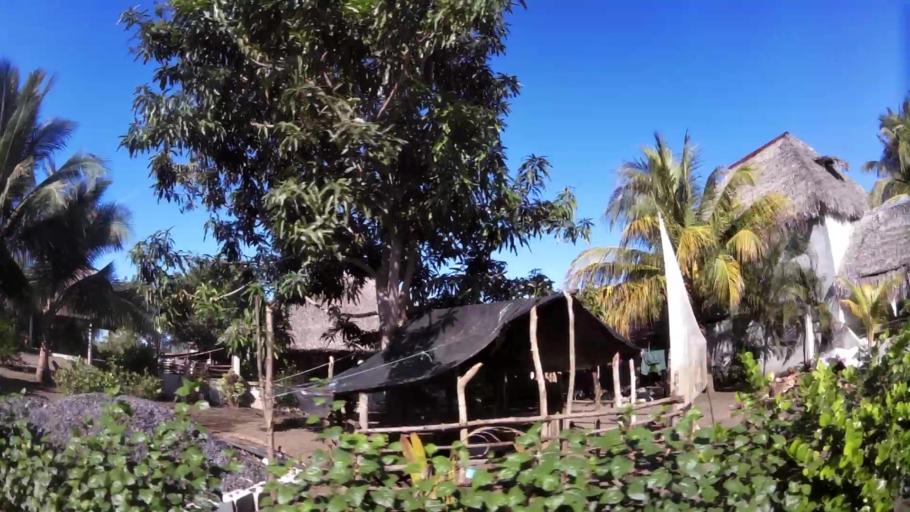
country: GT
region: Santa Rosa
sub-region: Municipio de Taxisco
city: Taxisco
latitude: 13.8953
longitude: -90.4901
